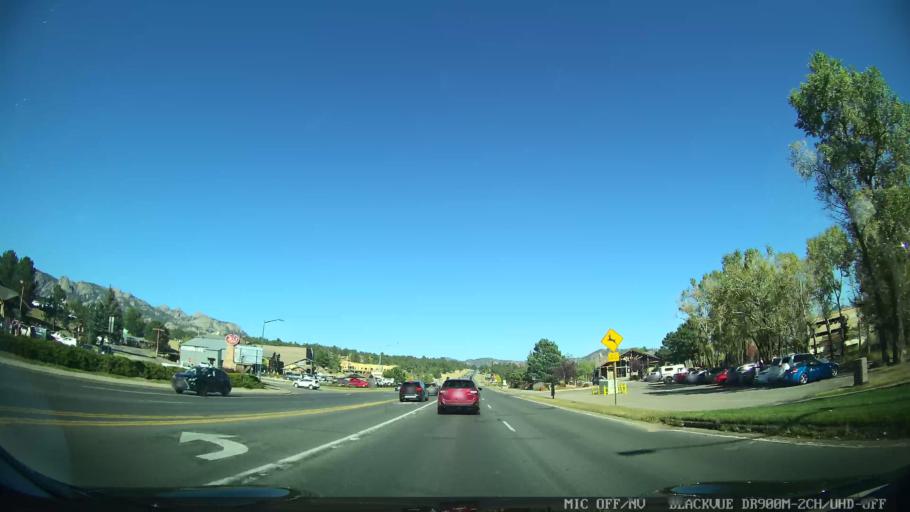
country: US
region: Colorado
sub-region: Larimer County
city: Estes Park
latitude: 40.3785
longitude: -105.5161
